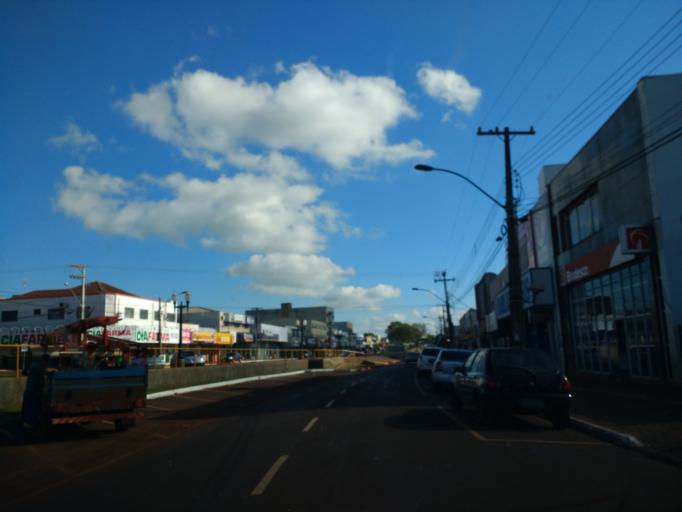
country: BR
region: Parana
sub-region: Palotina
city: Palotina
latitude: -24.4070
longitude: -53.5150
